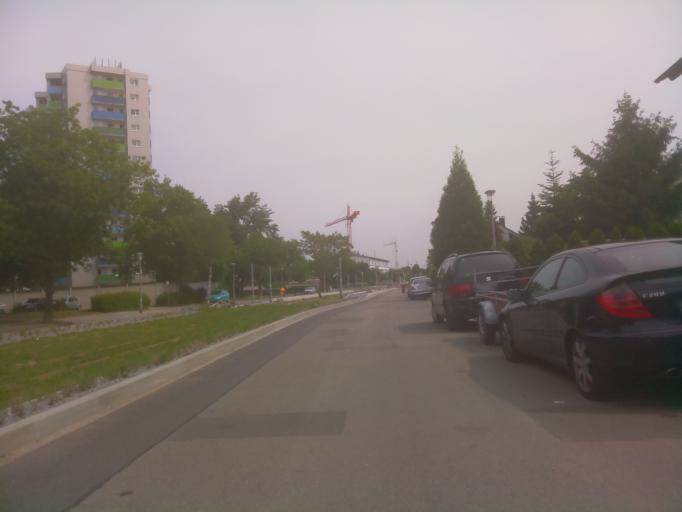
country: DE
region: Baden-Wuerttemberg
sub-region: Karlsruhe Region
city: Mannheim
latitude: 49.5221
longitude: 8.5002
